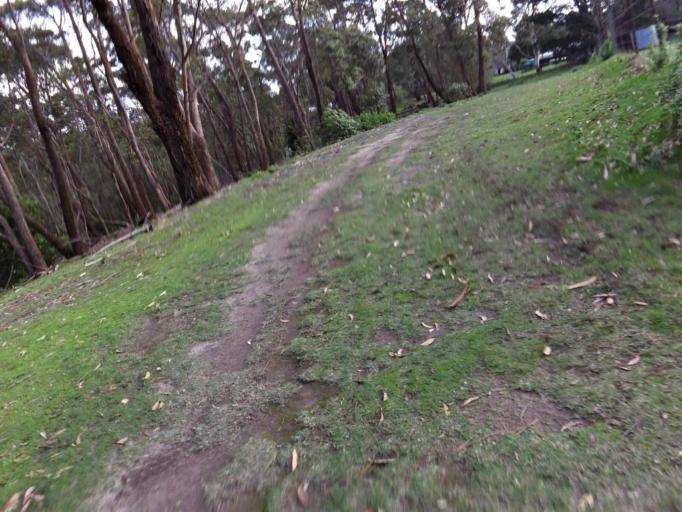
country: AU
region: Victoria
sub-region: Yarra Ranges
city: Lysterfield
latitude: -37.9582
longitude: 145.2899
